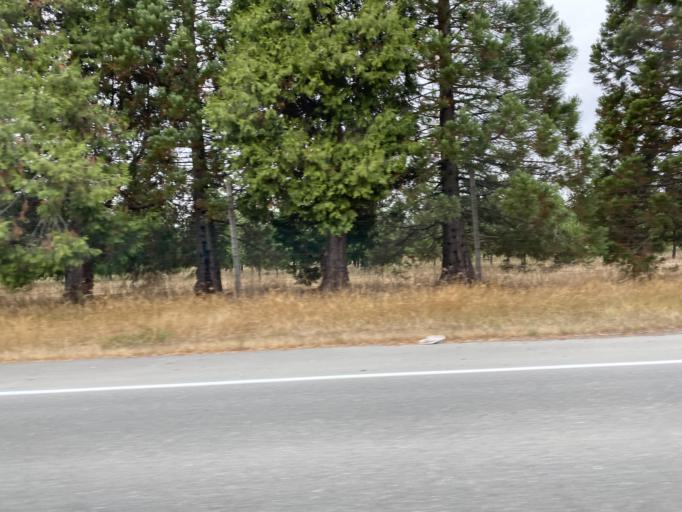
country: US
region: Washington
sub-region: Island County
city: Coupeville
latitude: 48.2112
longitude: -122.6345
